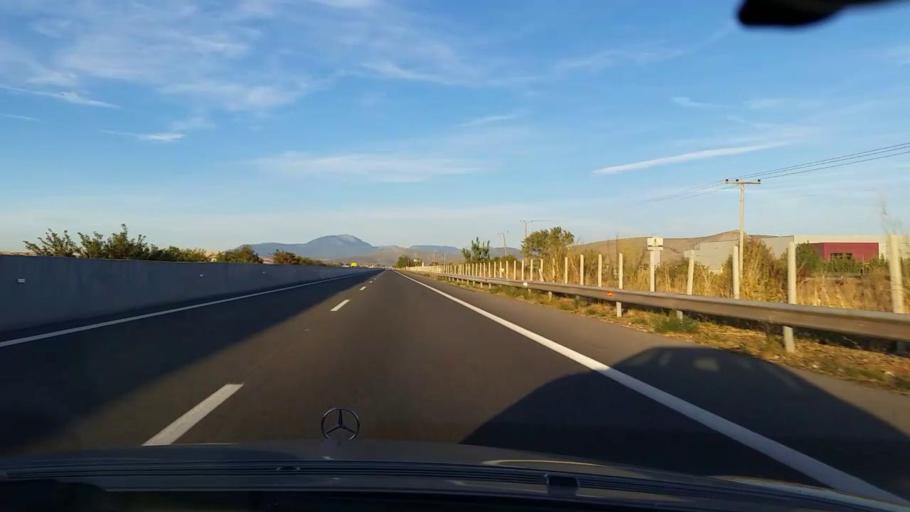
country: GR
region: Central Greece
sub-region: Nomos Voiotias
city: Thivai
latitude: 38.3697
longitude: 23.3738
